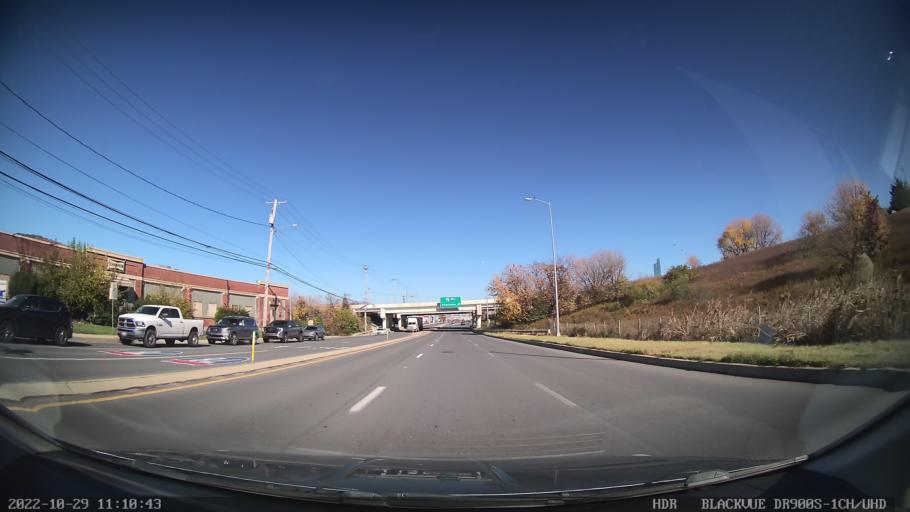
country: US
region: Pennsylvania
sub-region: Northampton County
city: Hellertown
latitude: 40.5952
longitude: -75.3403
